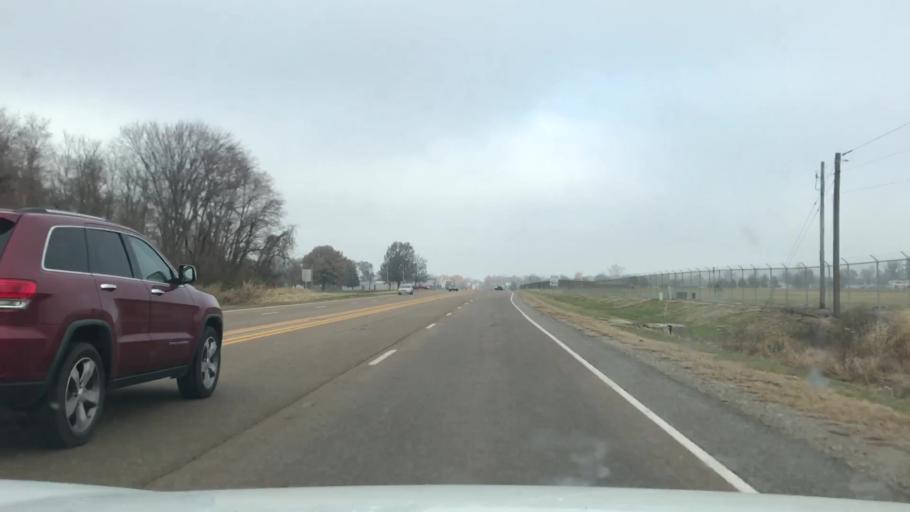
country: US
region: Illinois
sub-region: Madison County
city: Bethalto
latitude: 38.8947
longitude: -90.0593
